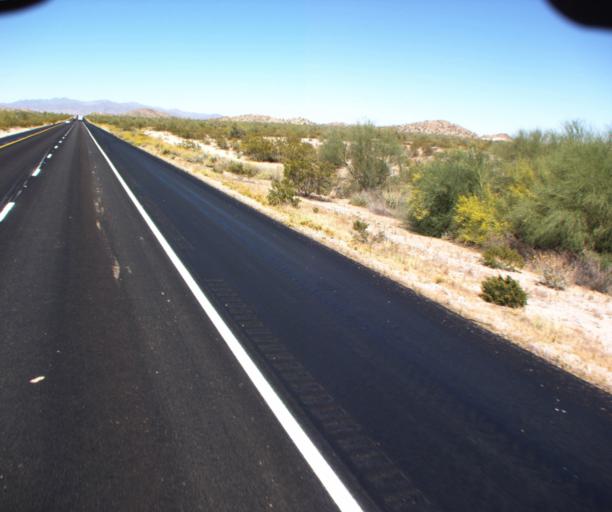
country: US
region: Arizona
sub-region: Maricopa County
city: Buckeye
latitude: 33.2798
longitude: -112.6309
